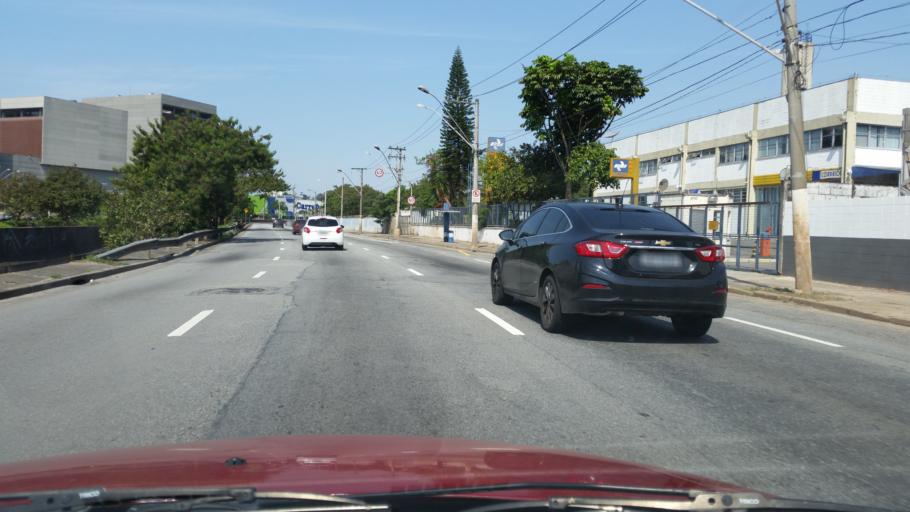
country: BR
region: Sao Paulo
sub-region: Santo Andre
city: Santo Andre
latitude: -23.6449
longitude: -46.5312
